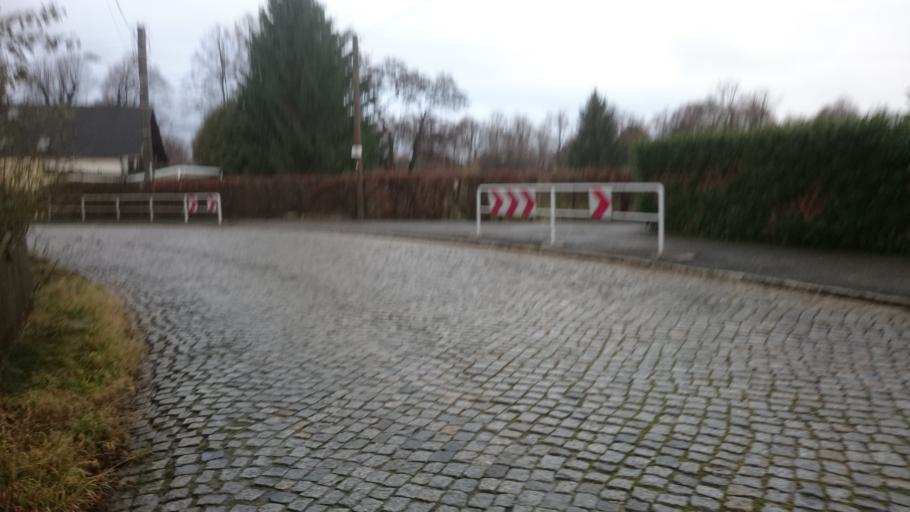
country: DE
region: Saxony
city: Zwickau
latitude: 50.7419
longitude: 12.4933
